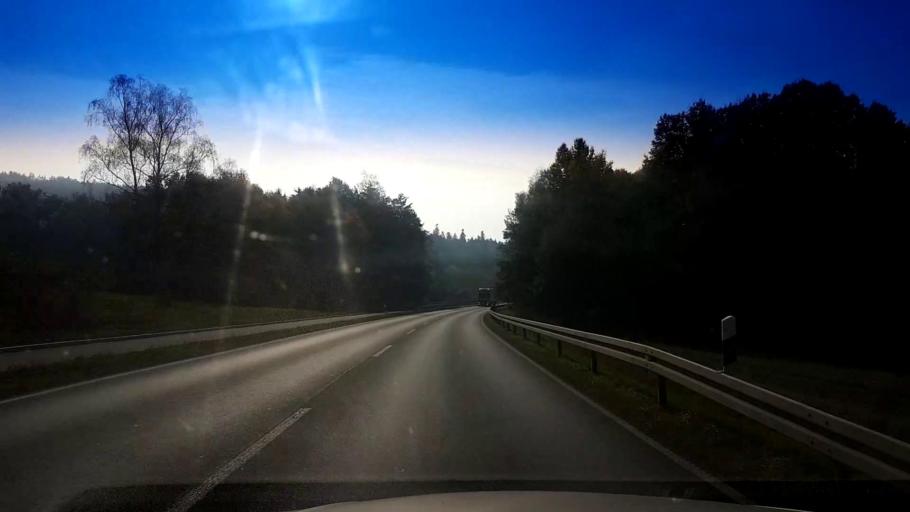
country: DE
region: Bavaria
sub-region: Upper Franconia
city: Neuenmarkt
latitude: 50.0909
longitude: 11.6091
